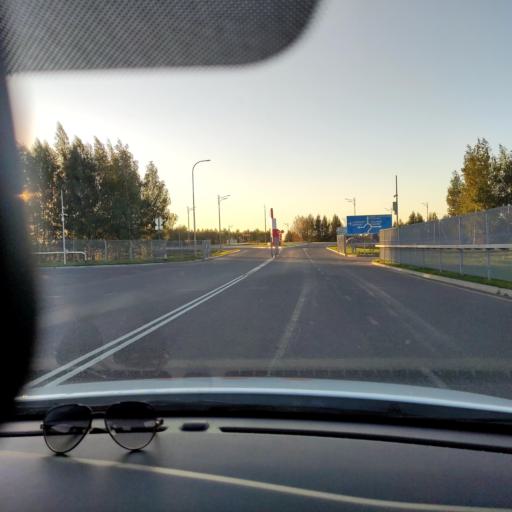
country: RU
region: Tatarstan
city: Stolbishchi
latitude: 55.6182
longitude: 49.2927
